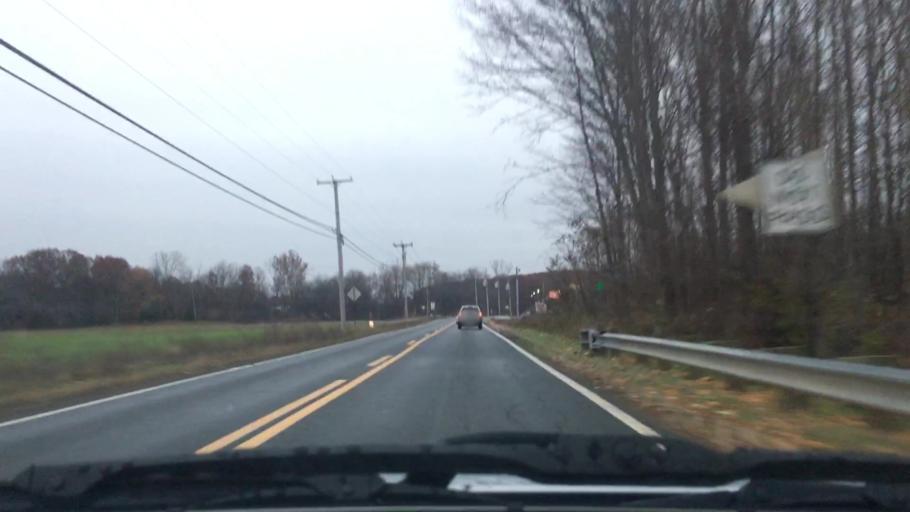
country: US
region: Massachusetts
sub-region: Hampden County
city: Southwick
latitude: 42.0739
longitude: -72.7673
